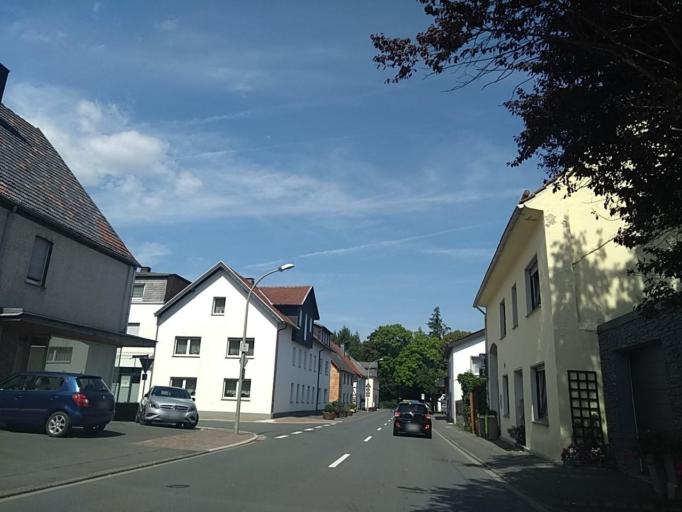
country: DE
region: North Rhine-Westphalia
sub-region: Regierungsbezirk Arnsberg
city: Brilon
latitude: 51.4578
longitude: 8.6264
